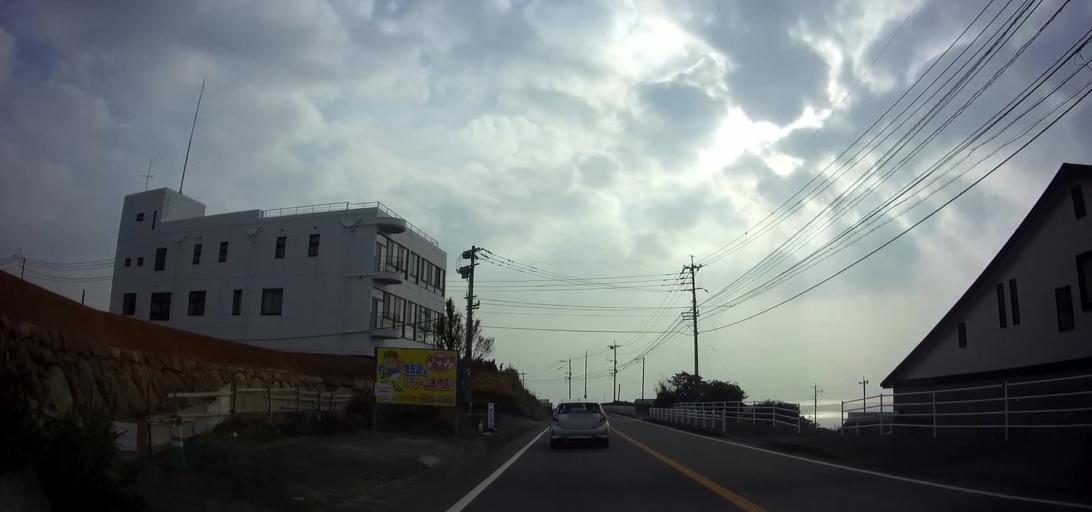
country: JP
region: Nagasaki
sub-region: Isahaya-shi
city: Isahaya
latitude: 32.7906
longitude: 130.0657
